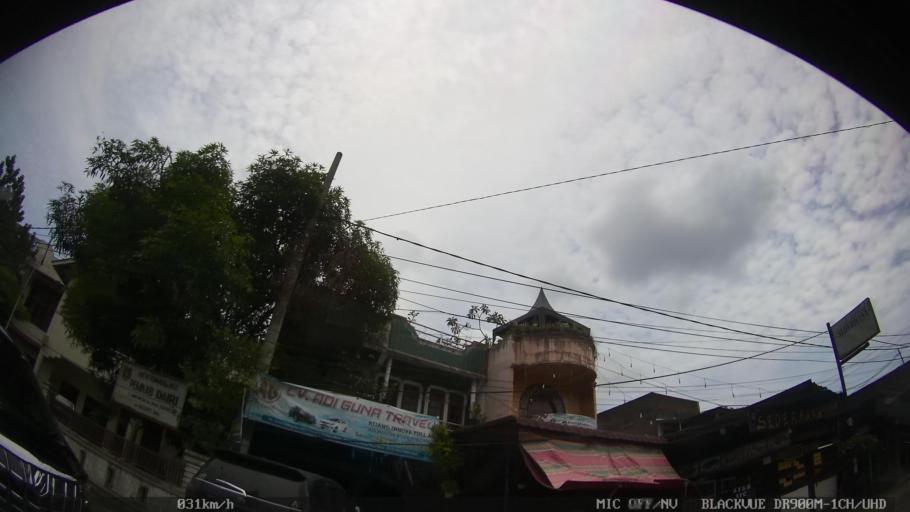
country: ID
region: North Sumatra
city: Medan
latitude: 3.5466
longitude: 98.6586
